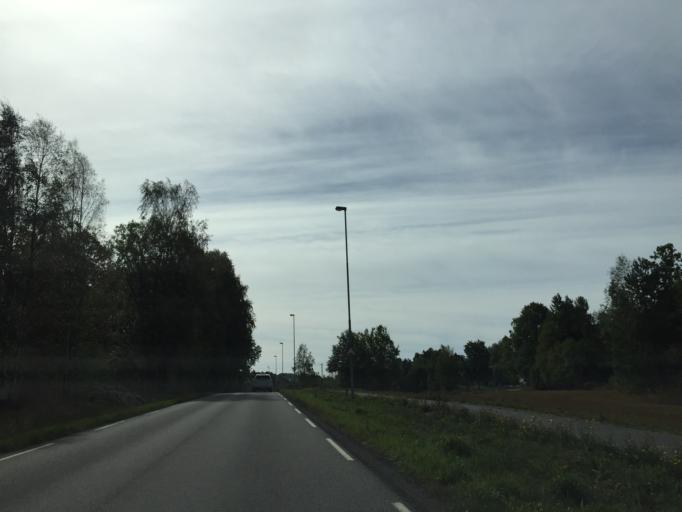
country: NO
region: Ostfold
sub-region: Moss
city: Moss
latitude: 59.4976
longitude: 10.6873
